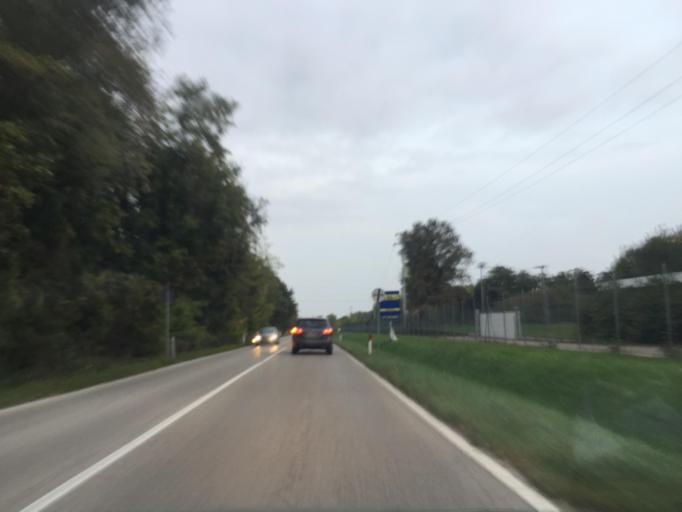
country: IT
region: Friuli Venezia Giulia
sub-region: Provincia di Pordenone
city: Fanna
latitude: 46.1732
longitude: 12.7346
